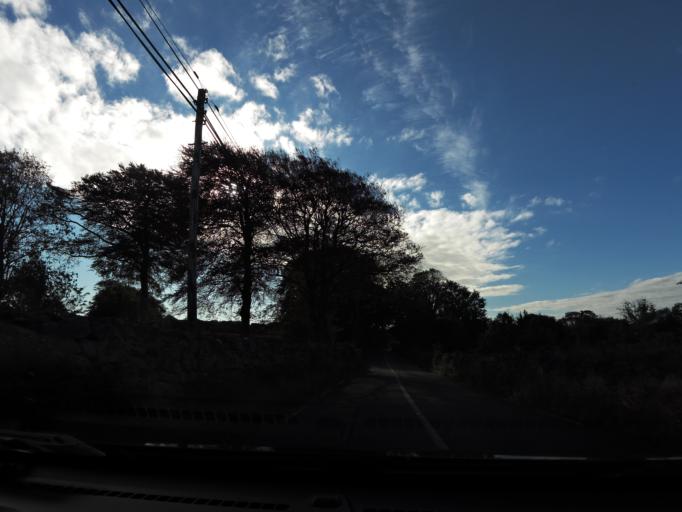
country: IE
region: Connaught
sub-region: County Galway
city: Athenry
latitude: 53.3052
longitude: -8.7705
